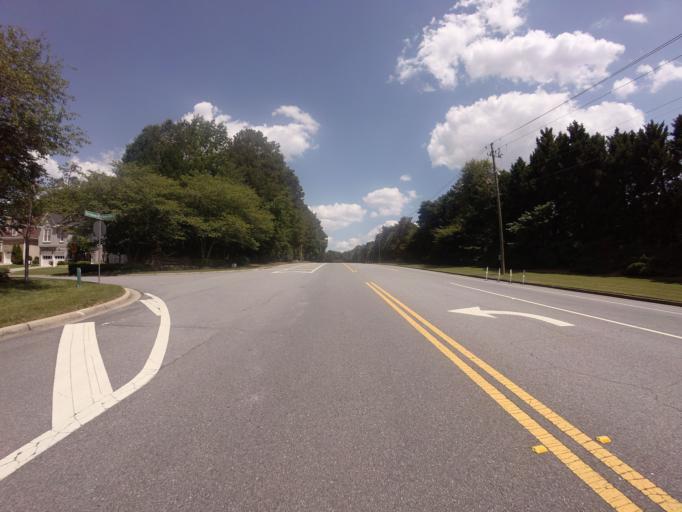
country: US
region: Georgia
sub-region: Fulton County
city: Johns Creek
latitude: 34.0098
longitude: -84.2174
